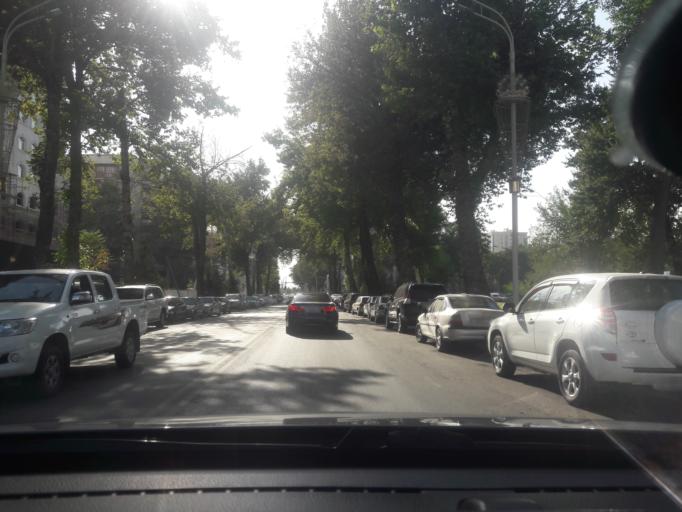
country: TJ
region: Dushanbe
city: Dushanbe
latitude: 38.5812
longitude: 68.7891
